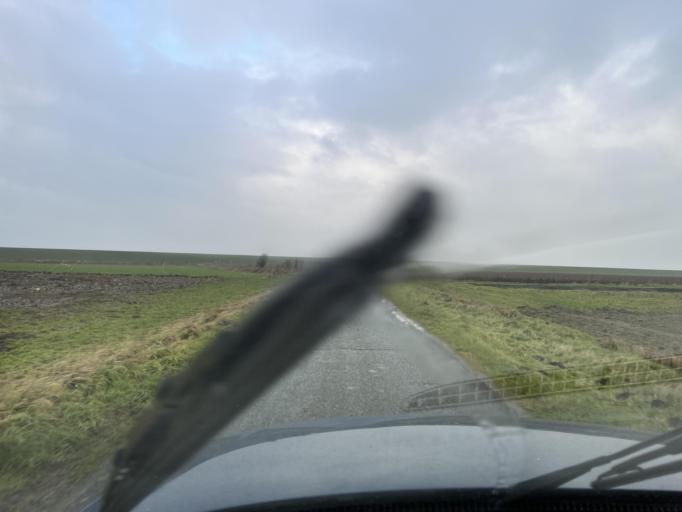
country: DE
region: Schleswig-Holstein
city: Hellschen-Heringsand-Unterschaar
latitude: 54.2238
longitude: 8.8465
